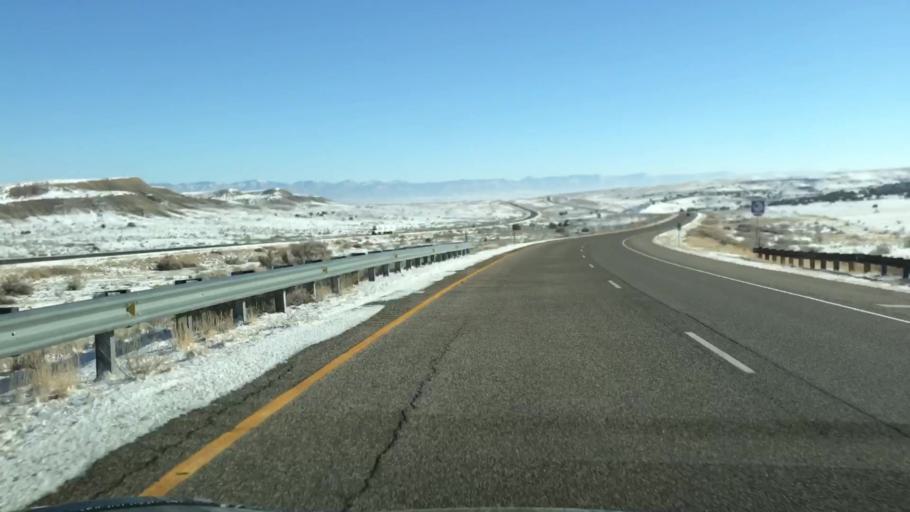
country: US
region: Colorado
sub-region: Mesa County
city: Loma
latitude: 39.2211
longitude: -108.9557
